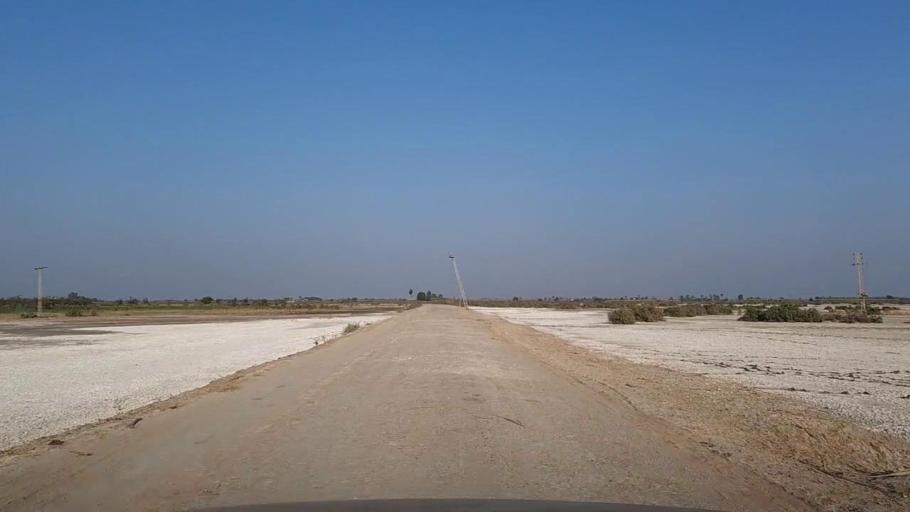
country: PK
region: Sindh
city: Tando Mittha Khan
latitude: 25.9304
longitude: 69.0663
